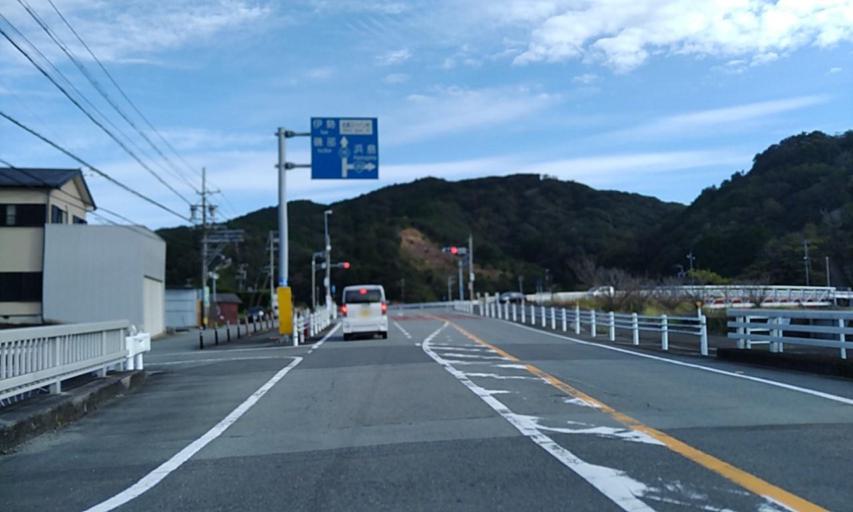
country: JP
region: Mie
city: Ise
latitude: 34.3436
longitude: 136.7264
